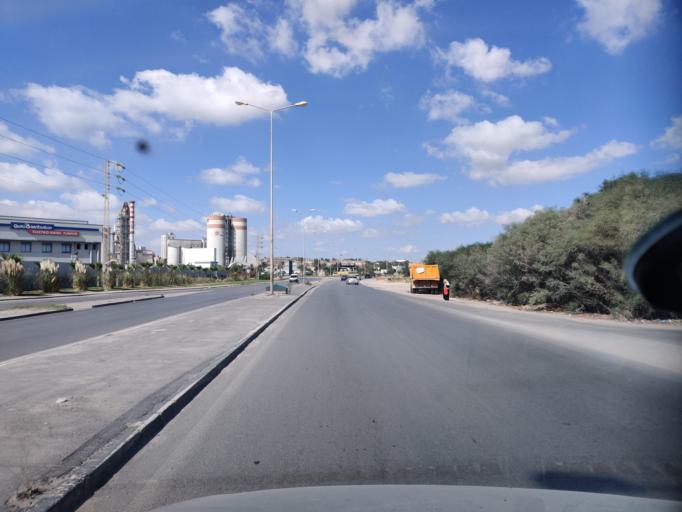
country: TN
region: Bin 'Arus
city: Ben Arous
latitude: 36.7773
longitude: 10.2086
